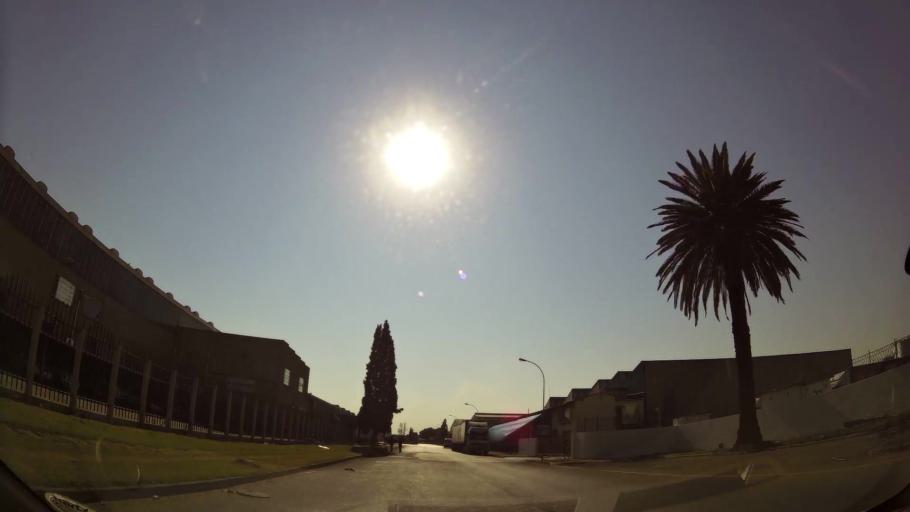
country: ZA
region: Gauteng
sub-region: City of Johannesburg Metropolitan Municipality
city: Modderfontein
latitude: -26.1436
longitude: 28.2065
